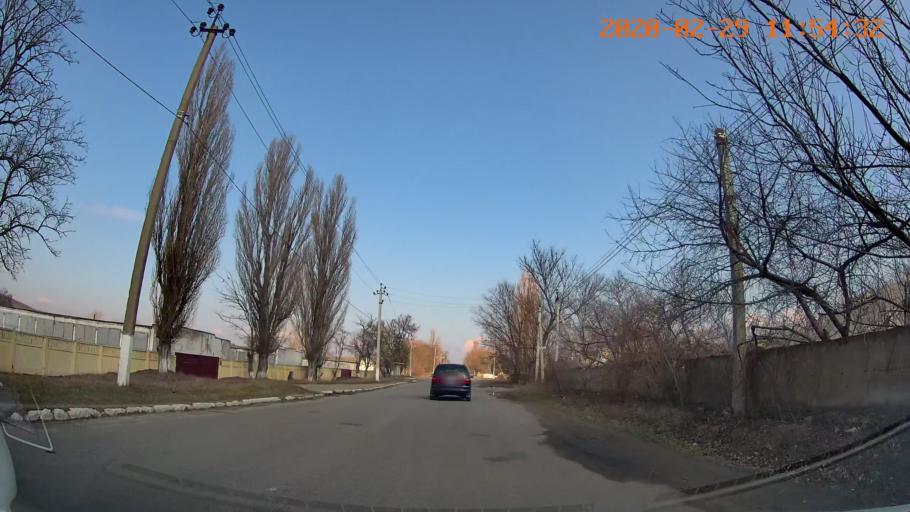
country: MD
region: Telenesti
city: Ribnita
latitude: 47.7849
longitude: 28.9954
